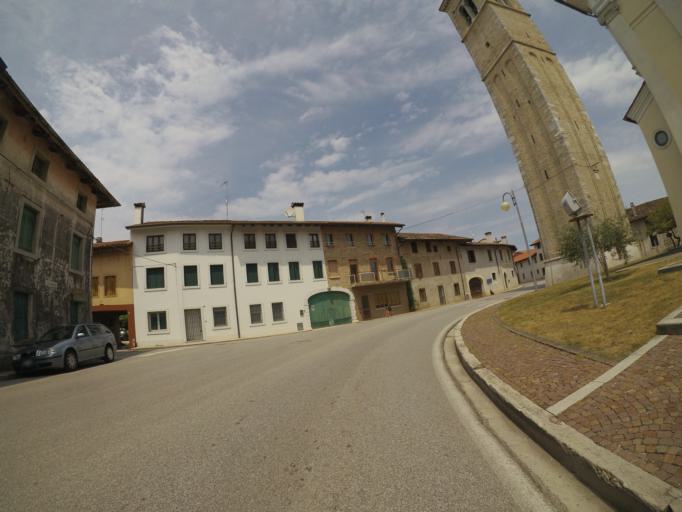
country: IT
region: Friuli Venezia Giulia
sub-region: Provincia di Udine
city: Sedegliano
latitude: 45.9994
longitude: 12.9978
